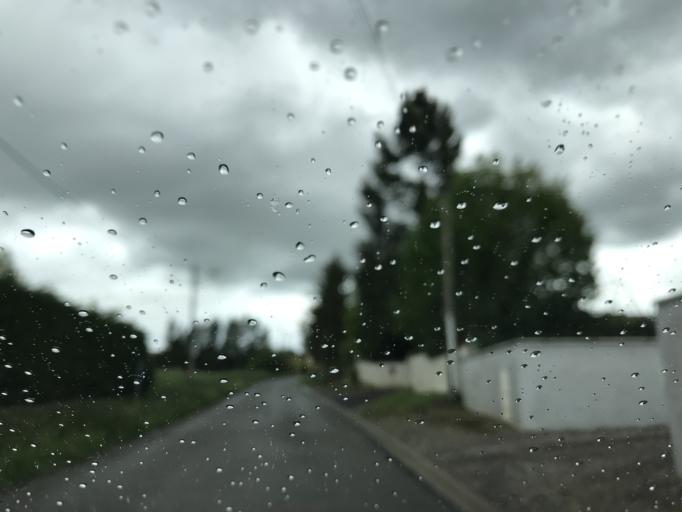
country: FR
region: Auvergne
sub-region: Departement du Puy-de-Dome
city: Billom
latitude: 45.7511
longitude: 3.3390
